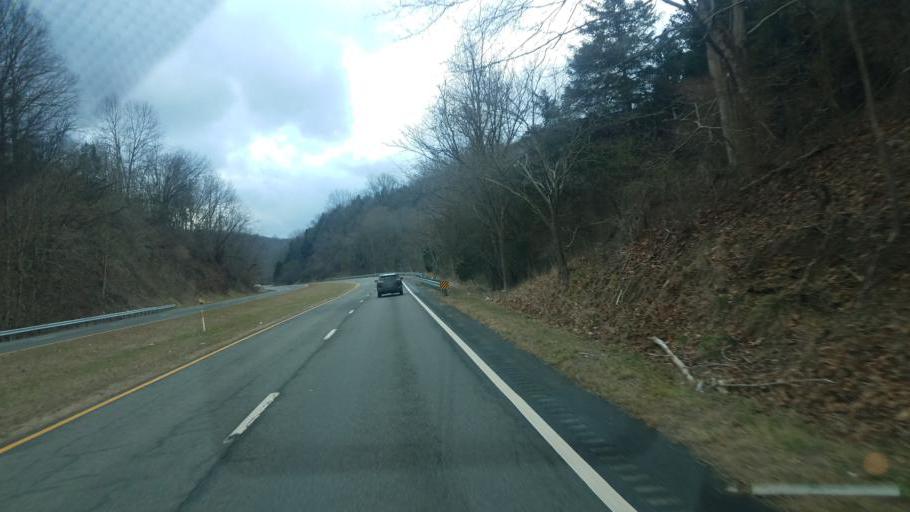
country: US
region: Virginia
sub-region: Giles County
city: Pearisburg
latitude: 37.2704
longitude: -80.7208
